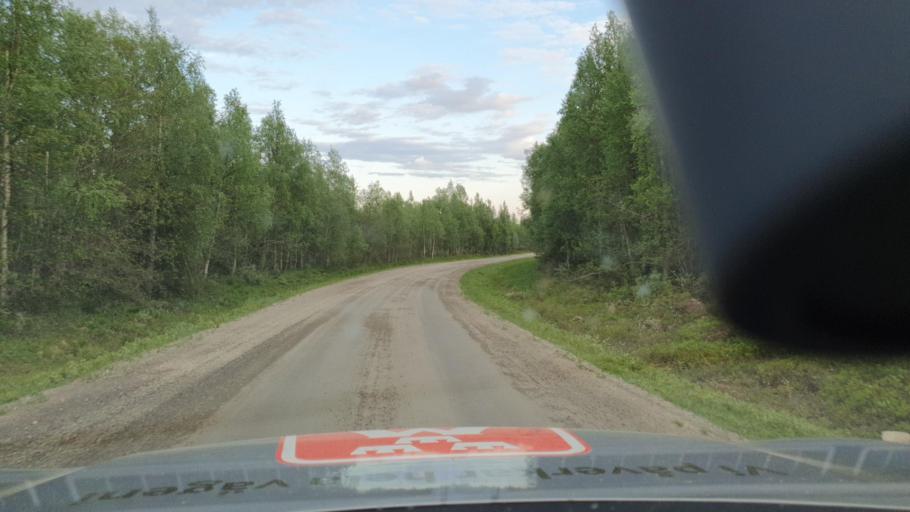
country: SE
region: Norrbotten
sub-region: Bodens Kommun
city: Boden
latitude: 66.6156
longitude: 21.3530
